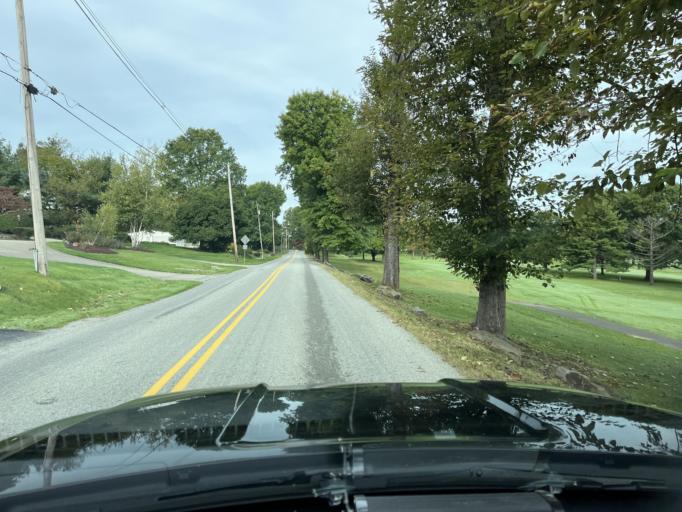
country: US
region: Pennsylvania
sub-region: Fayette County
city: Leith-Hatfield
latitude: 39.8843
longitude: -79.7234
